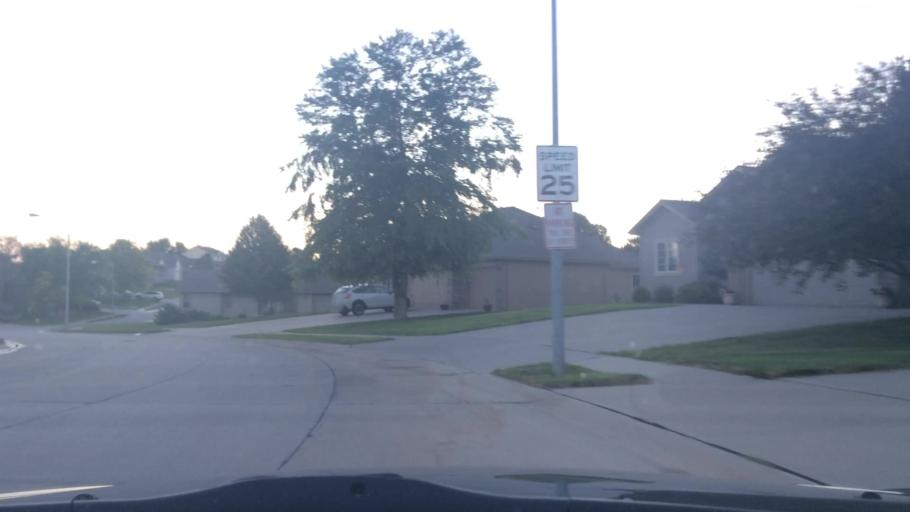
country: US
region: Nebraska
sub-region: Douglas County
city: Ralston
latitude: 41.1857
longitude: -96.0606
